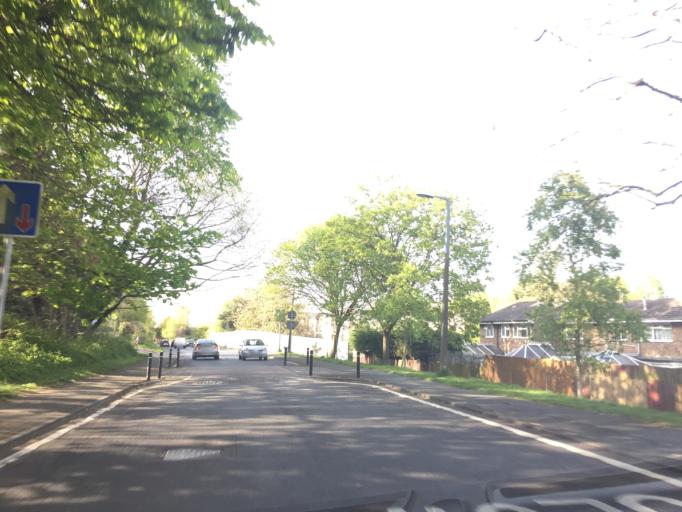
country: GB
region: England
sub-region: Essex
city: Harlow
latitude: 51.7488
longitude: 0.0843
